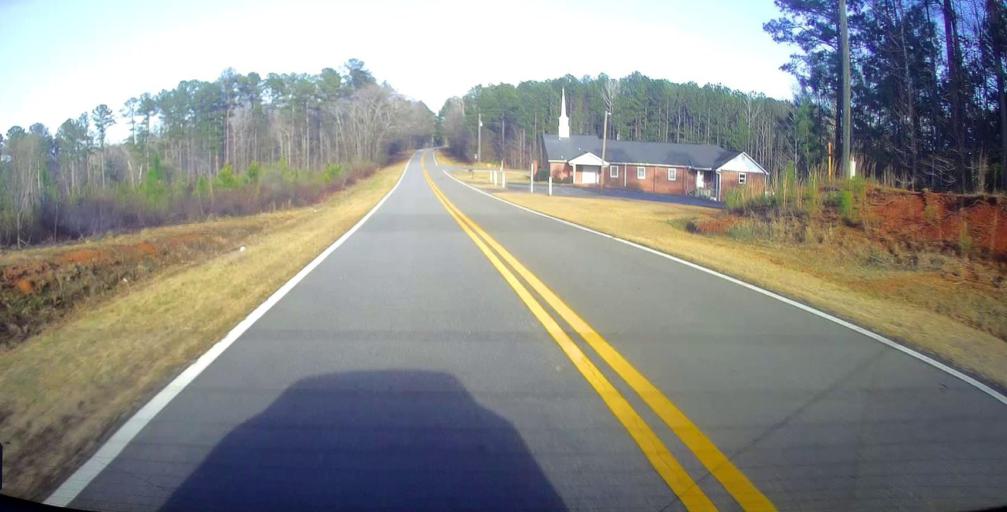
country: US
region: Georgia
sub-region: Crawford County
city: Knoxville
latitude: 32.8332
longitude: -83.9297
